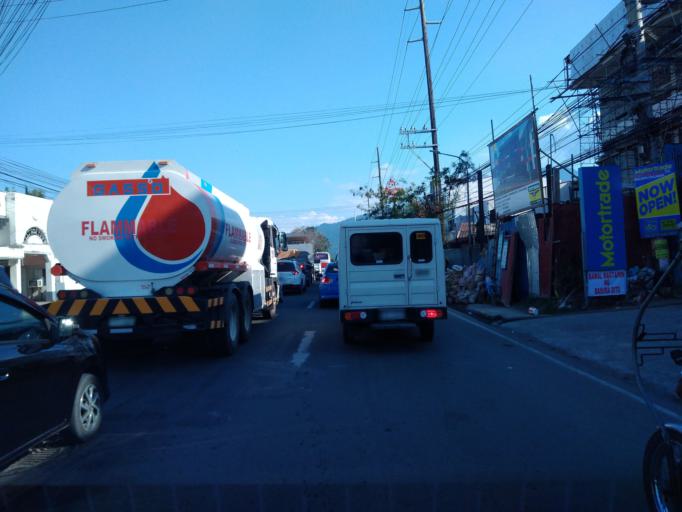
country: PH
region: Calabarzon
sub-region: Province of Laguna
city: Calamba
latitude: 14.1931
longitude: 121.1658
